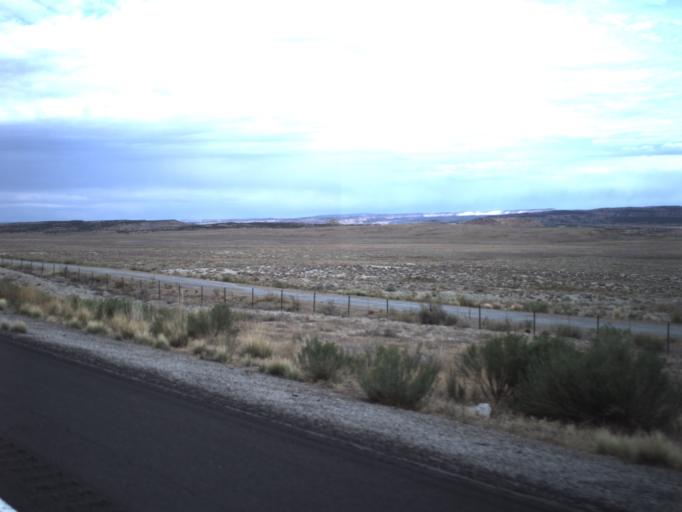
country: US
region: Colorado
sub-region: Mesa County
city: Loma
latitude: 39.0554
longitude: -109.2597
